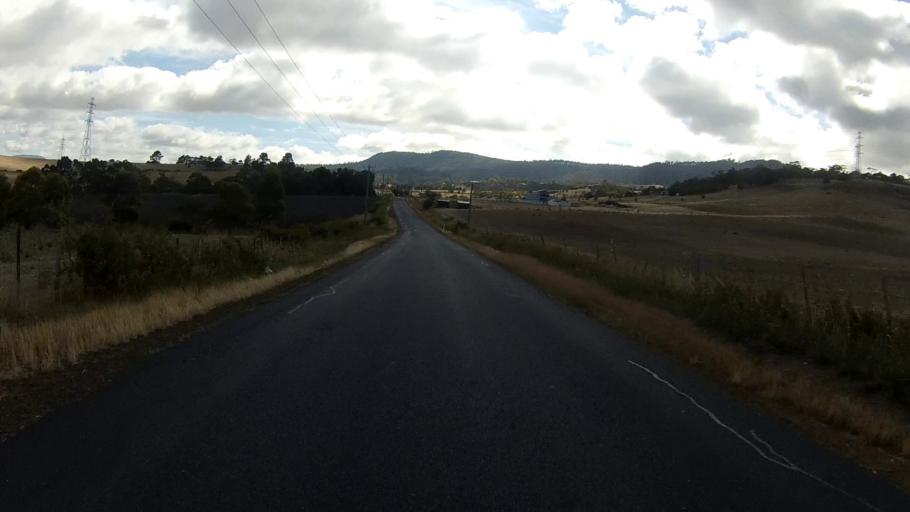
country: AU
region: Tasmania
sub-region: Brighton
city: Old Beach
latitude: -42.7707
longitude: 147.2929
